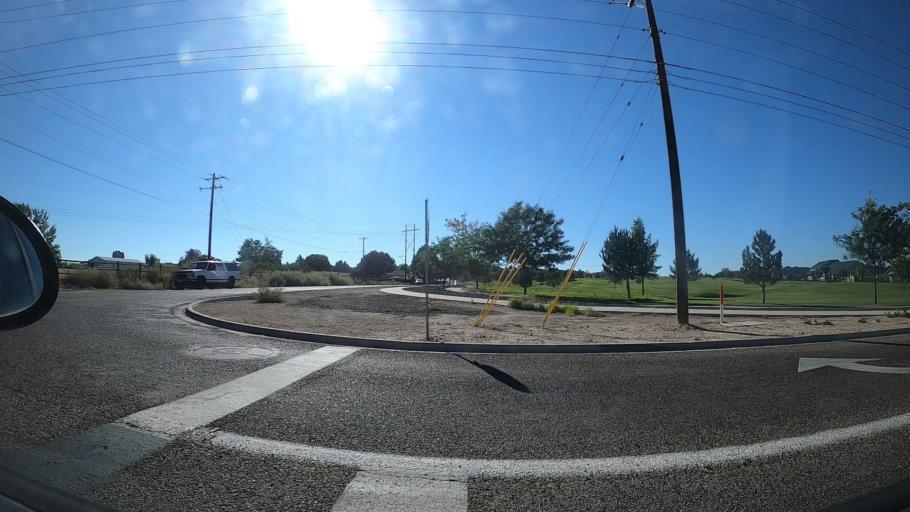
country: US
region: Idaho
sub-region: Canyon County
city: Nampa
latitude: 43.5486
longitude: -116.6126
